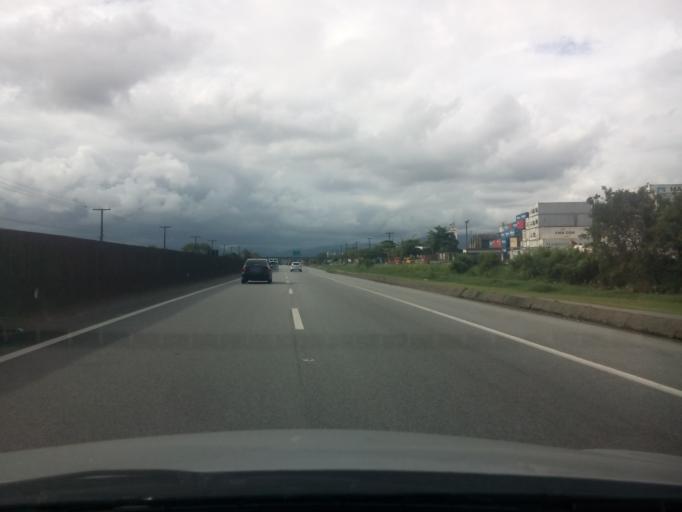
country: BR
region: Sao Paulo
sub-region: Guaruja
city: Guaruja
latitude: -23.9758
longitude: -46.2680
